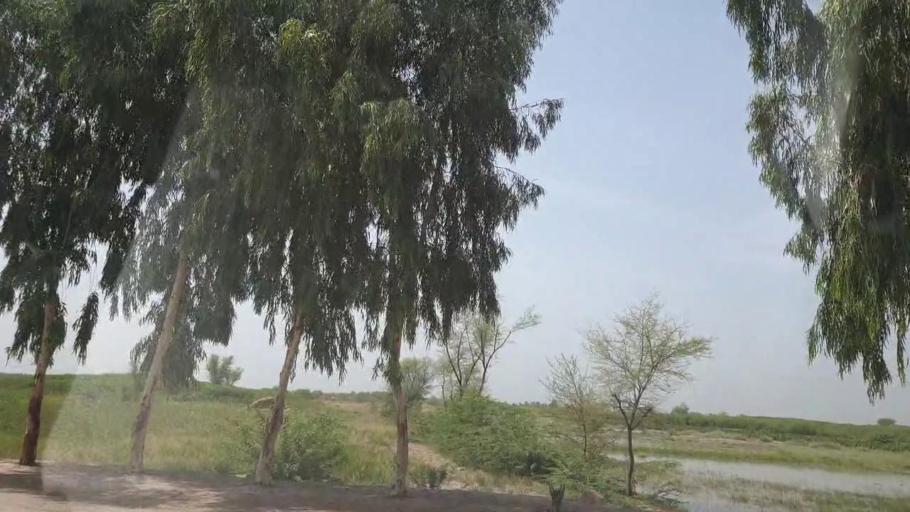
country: PK
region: Sindh
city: Gambat
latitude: 27.3139
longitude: 68.5408
